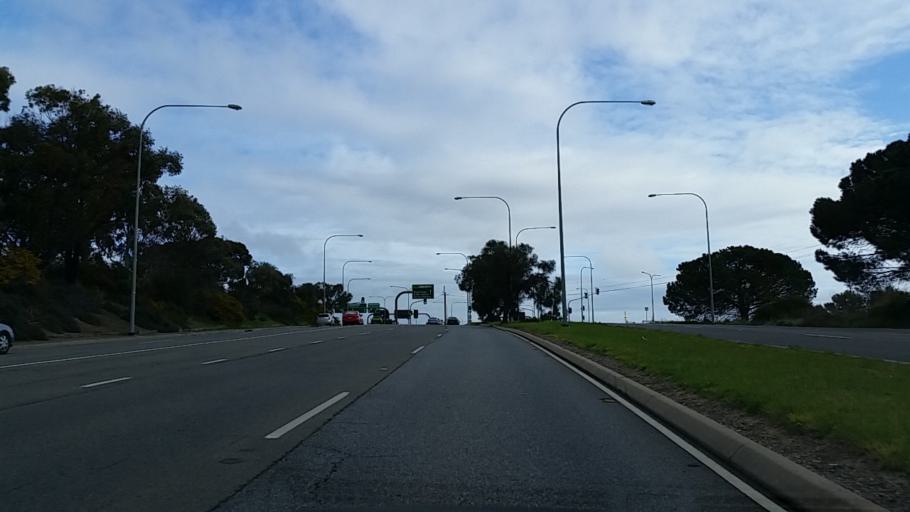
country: AU
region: South Australia
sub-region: Marion
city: Trott Park
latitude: -35.0796
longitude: 138.5473
